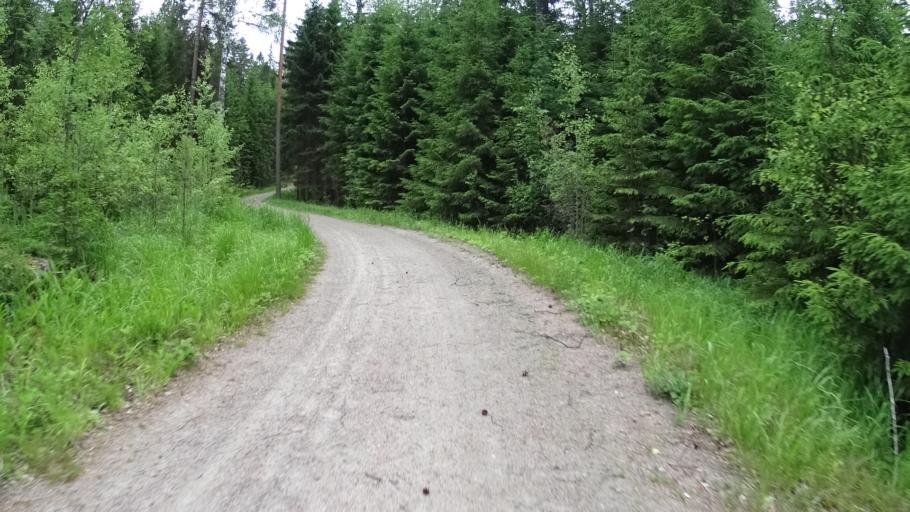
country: FI
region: Uusimaa
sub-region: Helsinki
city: Espoo
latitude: 60.2827
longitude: 24.6107
